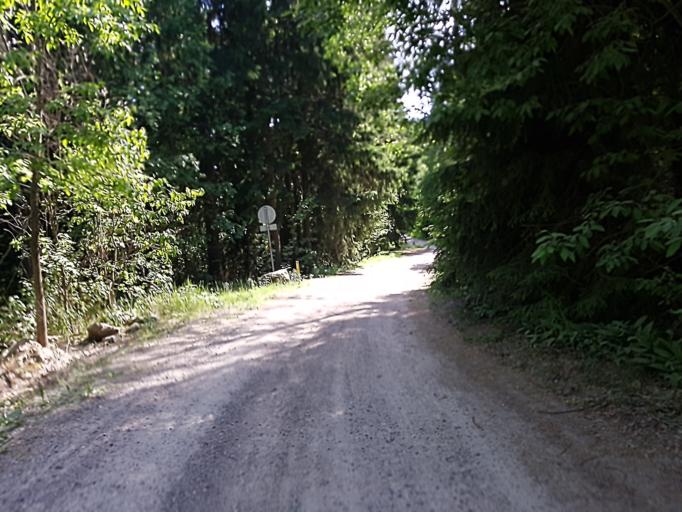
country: FI
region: Uusimaa
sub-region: Helsinki
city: Vantaa
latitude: 60.2938
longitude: 24.9177
